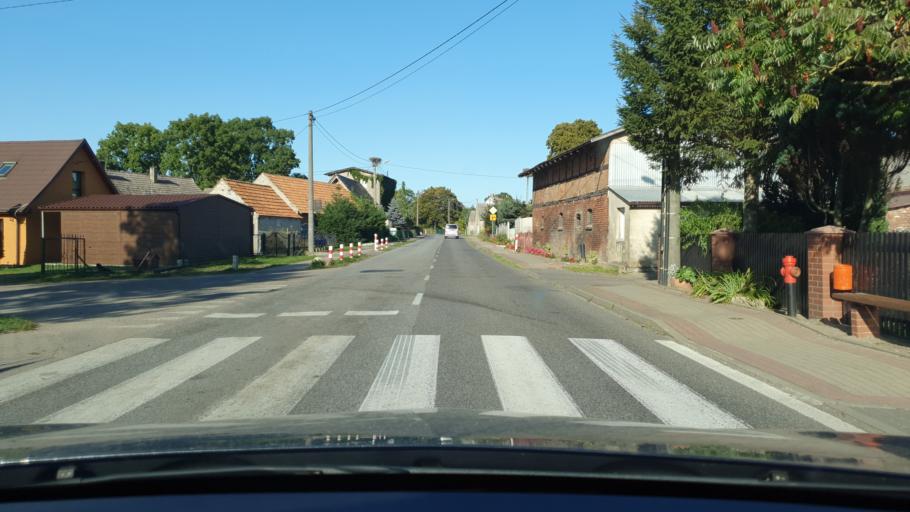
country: PL
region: West Pomeranian Voivodeship
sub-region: Powiat kamienski
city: Golczewo
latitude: 53.8326
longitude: 14.8787
